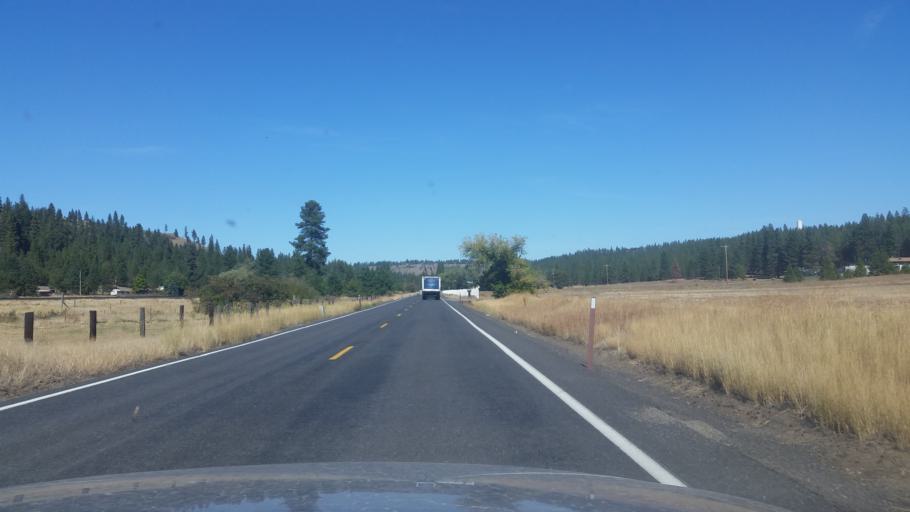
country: US
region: Washington
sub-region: Spokane County
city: Spokane
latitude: 47.5899
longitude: -117.4514
